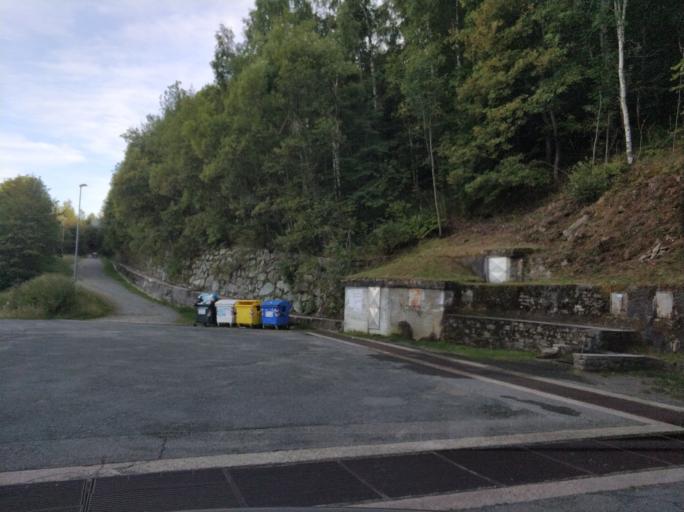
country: IT
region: Piedmont
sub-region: Provincia di Torino
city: Monastero di Lanzo
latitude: 45.3088
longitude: 7.4257
